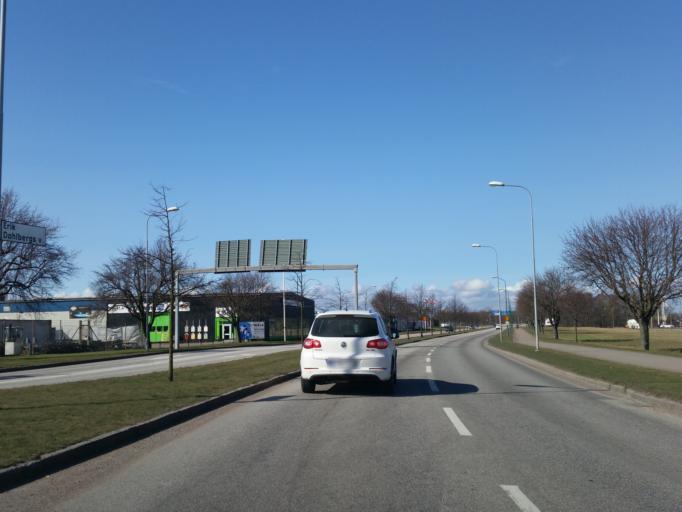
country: SE
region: Kalmar
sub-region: Kalmar Kommun
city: Kalmar
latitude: 56.6725
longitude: 16.3336
